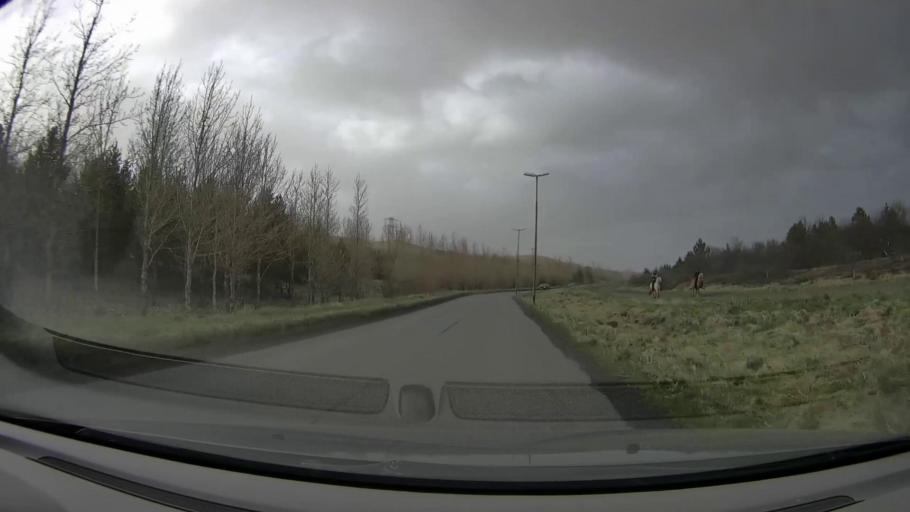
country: IS
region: Capital Region
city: Hafnarfjoerdur
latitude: 64.0454
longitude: -21.9199
